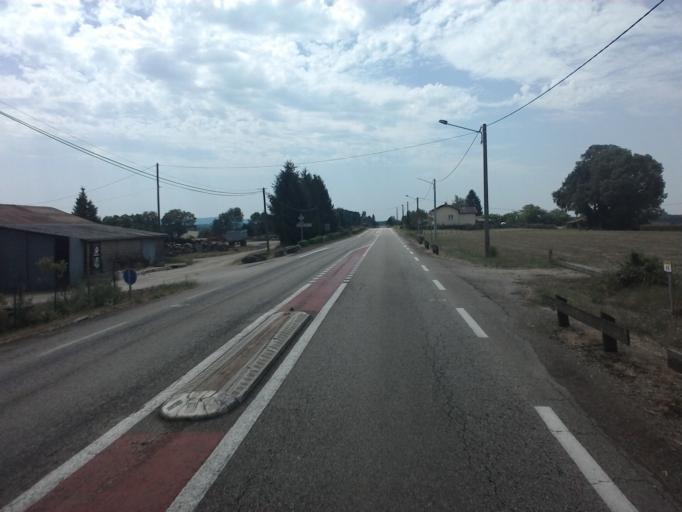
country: FR
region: Rhone-Alpes
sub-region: Departement de l'Ain
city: Coligny
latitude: 46.3446
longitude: 5.3203
